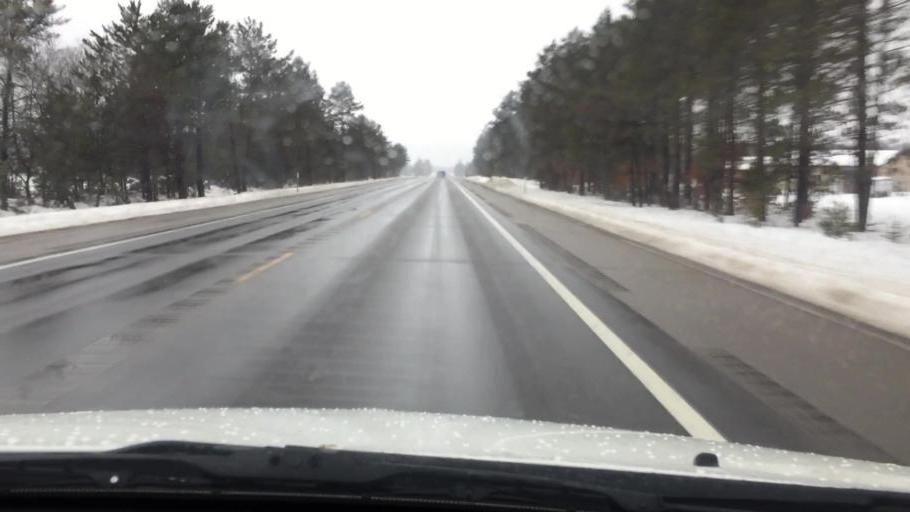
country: US
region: Michigan
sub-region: Kalkaska County
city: Kalkaska
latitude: 44.6839
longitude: -85.2239
